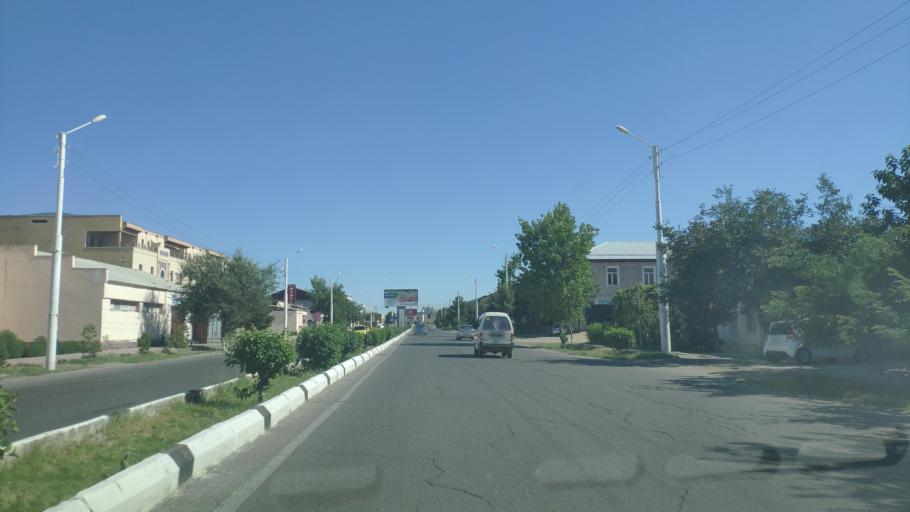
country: UZ
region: Bukhara
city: Bukhara
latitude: 39.7872
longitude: 64.4198
